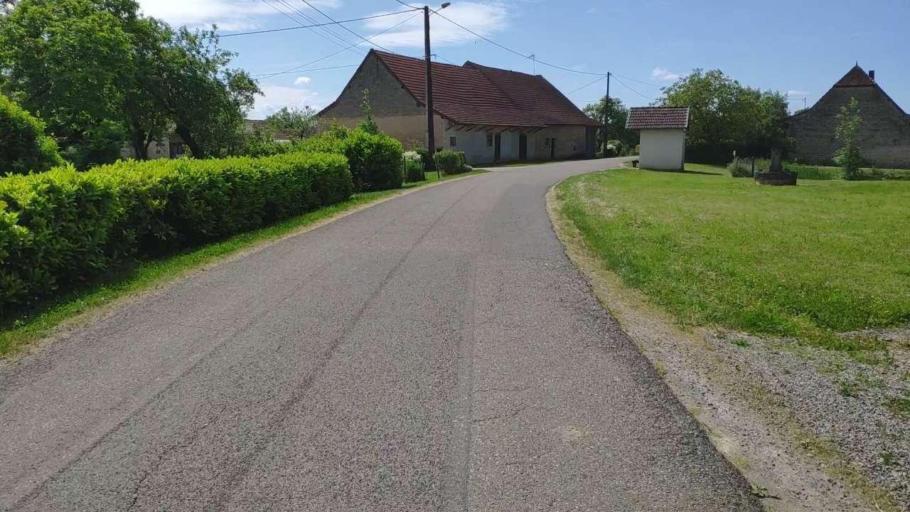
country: FR
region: Franche-Comte
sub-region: Departement du Jura
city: Bletterans
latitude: 46.7060
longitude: 5.4114
